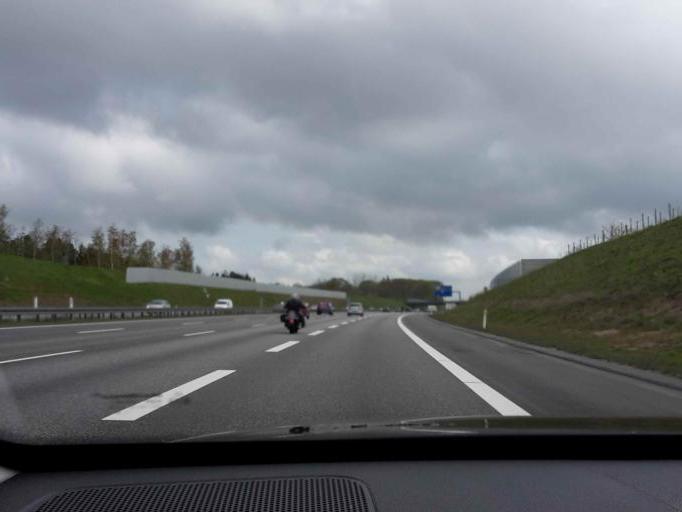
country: DK
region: South Denmark
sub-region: Vejle Kommune
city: Vejle
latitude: 55.6770
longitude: 9.5562
